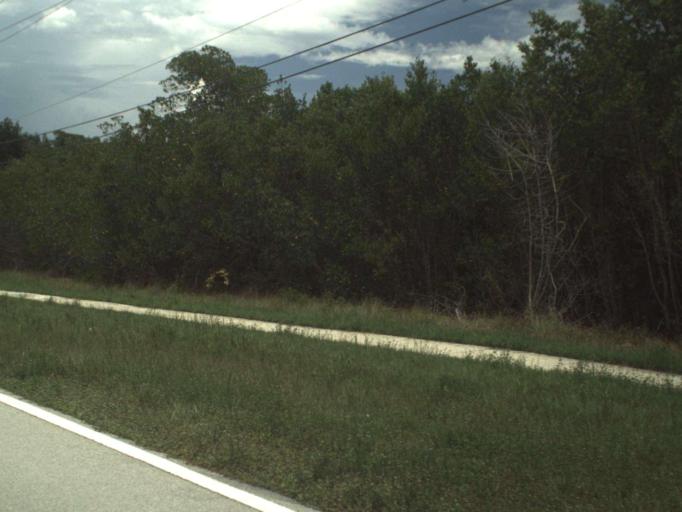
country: US
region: Florida
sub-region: Saint Lucie County
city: Hutchinson Island South
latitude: 27.3313
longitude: -80.2329
